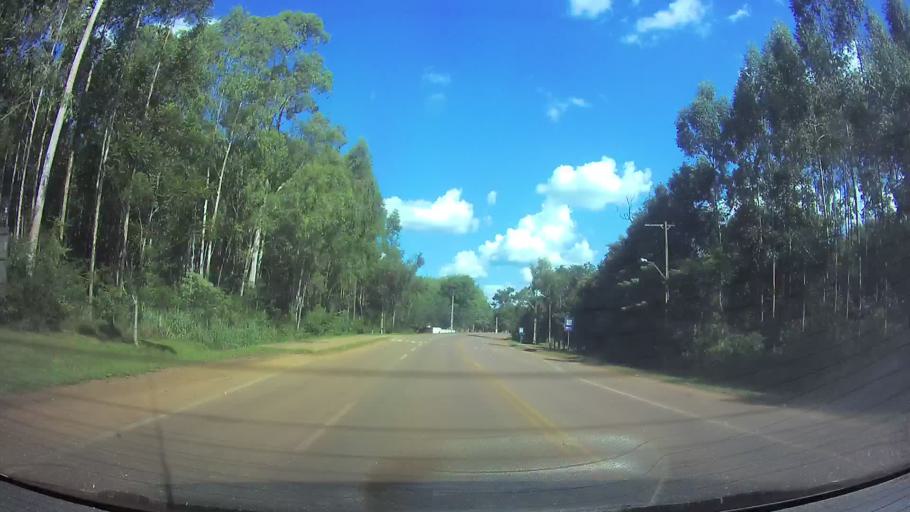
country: PY
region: Guaira
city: Coronel Martinez
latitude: -25.7683
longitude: -56.6527
